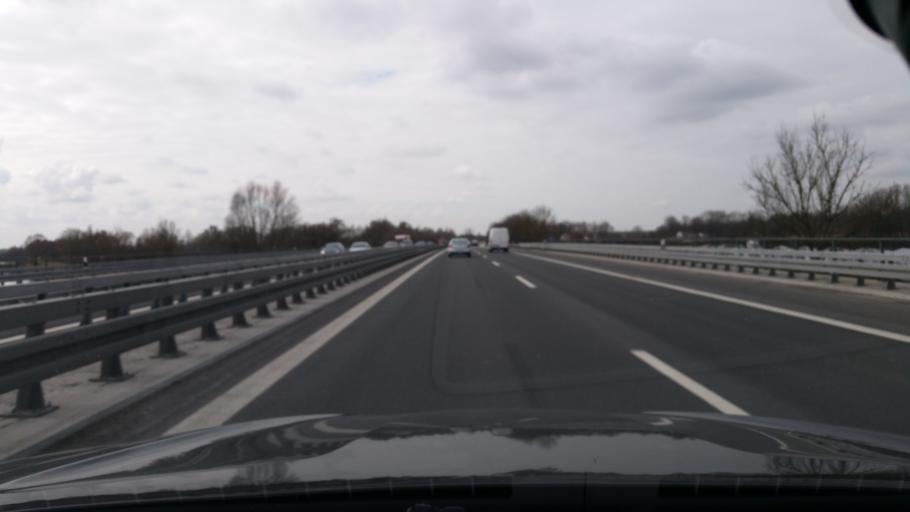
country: DE
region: Bavaria
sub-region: Upper Bavaria
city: Berglern
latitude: 48.4150
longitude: 11.9145
